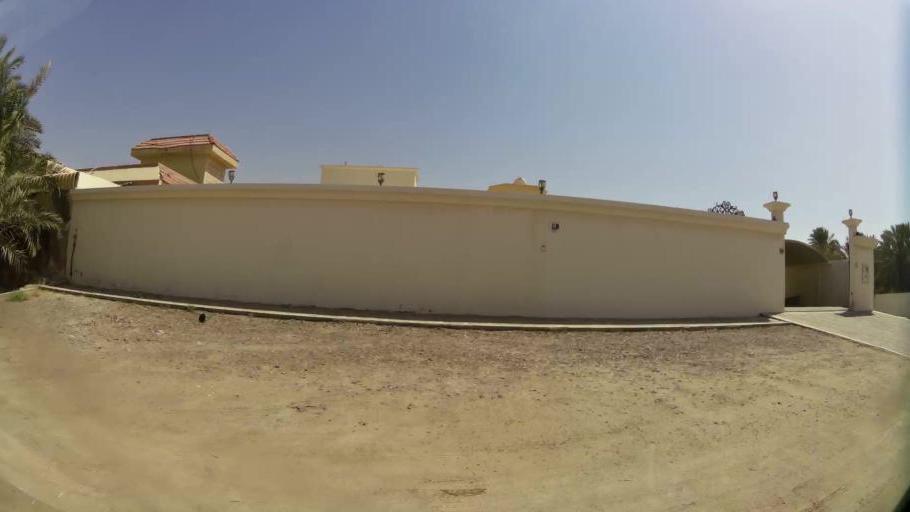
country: AE
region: Ajman
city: Ajman
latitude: 25.4134
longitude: 55.4795
